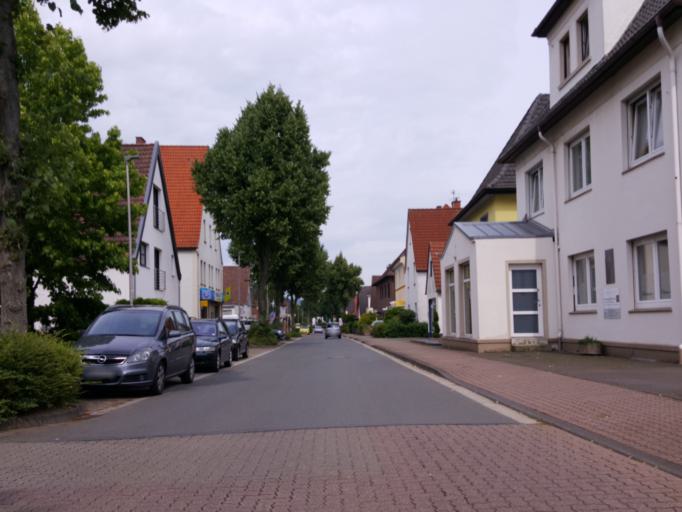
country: DE
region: North Rhine-Westphalia
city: Bad Oeynhausen
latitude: 52.2107
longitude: 8.8167
